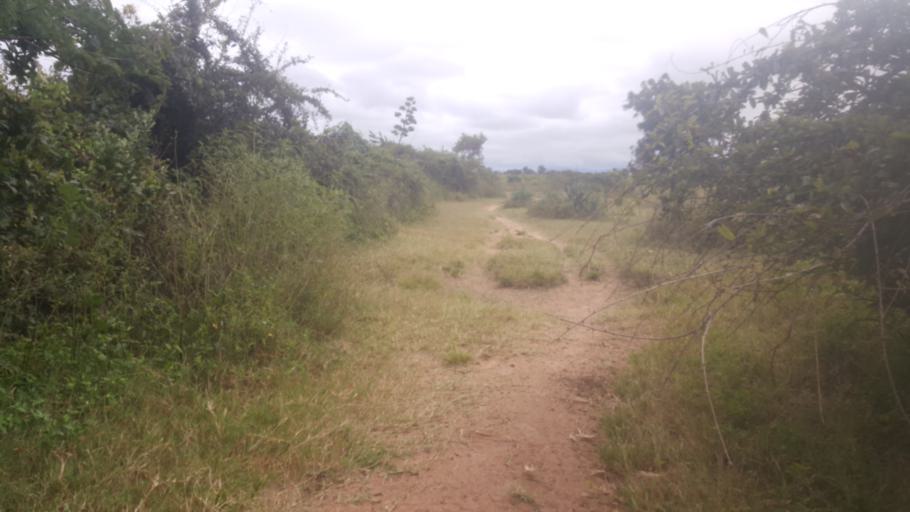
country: TZ
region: Dodoma
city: Msanga
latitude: -6.0382
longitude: 35.9380
